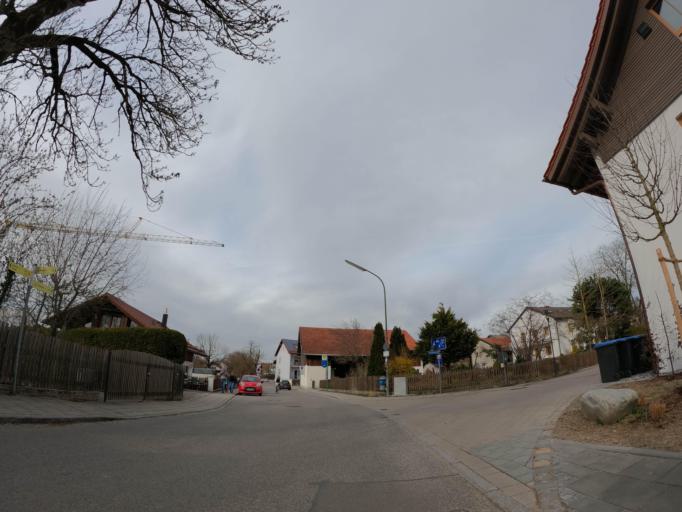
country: DE
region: Bavaria
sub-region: Upper Bavaria
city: Taufkirchen
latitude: 48.0409
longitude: 11.6217
